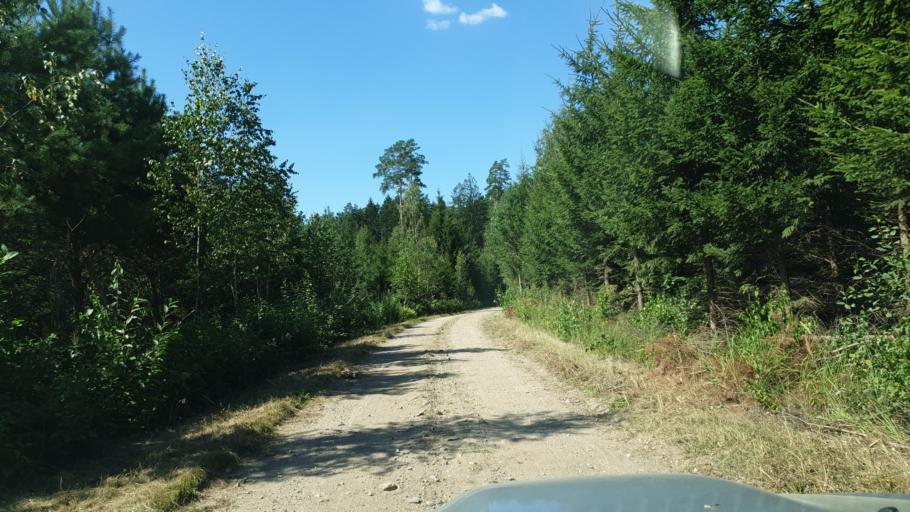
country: LT
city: Sirvintos
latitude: 54.9073
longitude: 24.9424
